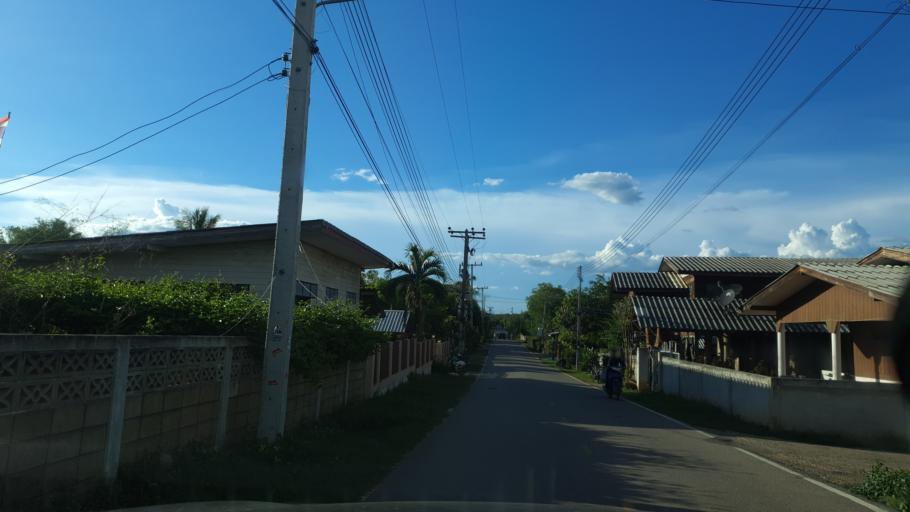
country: TH
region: Lampang
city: Sop Prap
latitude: 17.8858
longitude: 99.3115
